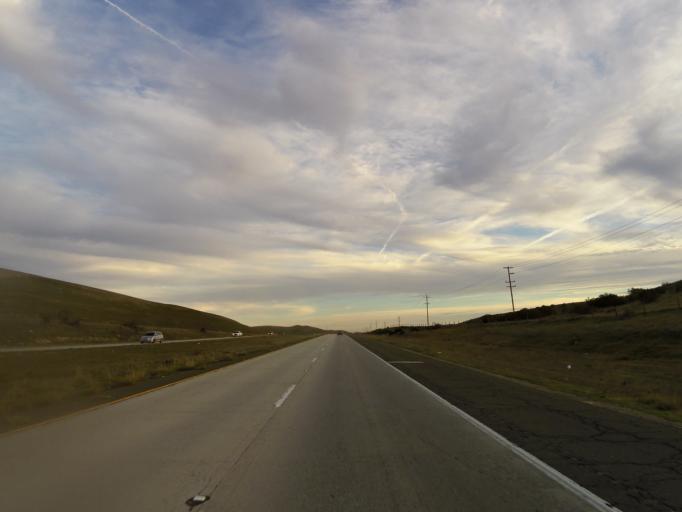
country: US
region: California
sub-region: Monterey County
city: King City
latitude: 36.1646
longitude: -121.0544
